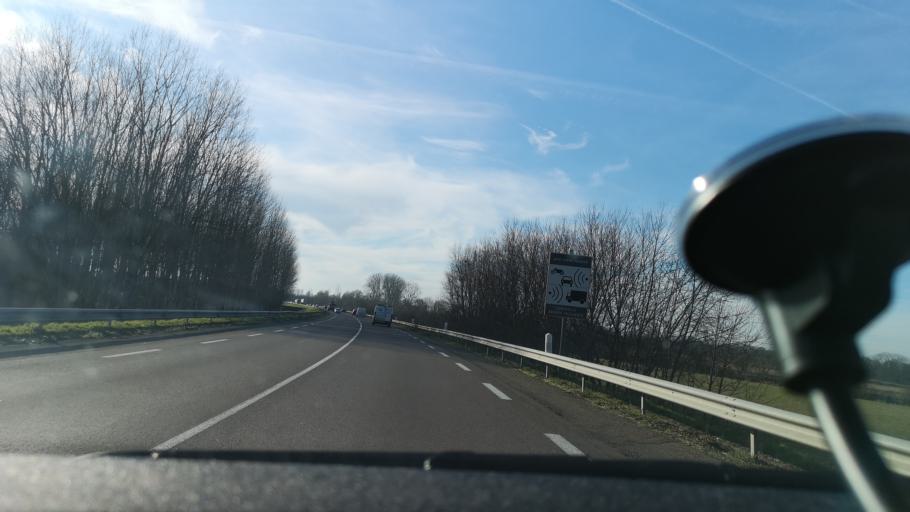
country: FR
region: Bourgogne
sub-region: Departement de Saone-et-Loire
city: Saint-Marcel
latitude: 46.7888
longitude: 4.8997
